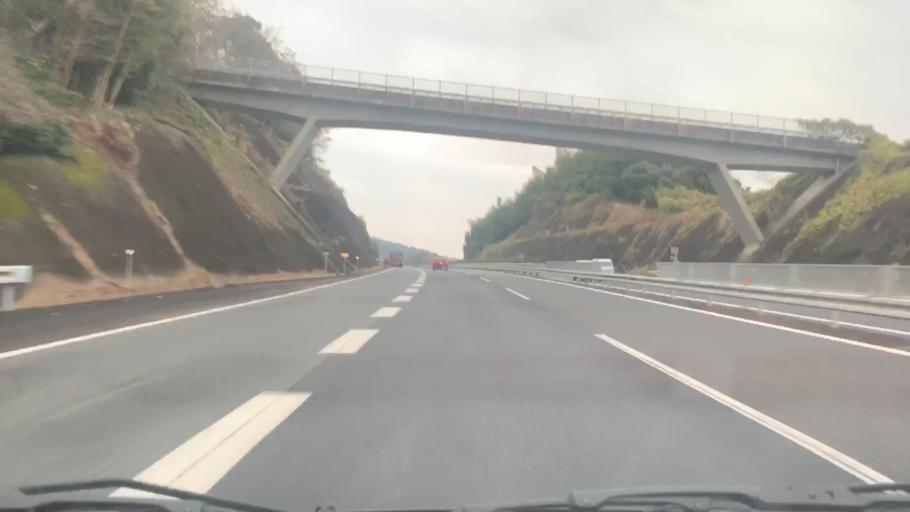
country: JP
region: Nagasaki
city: Omura
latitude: 32.9940
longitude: 129.9529
